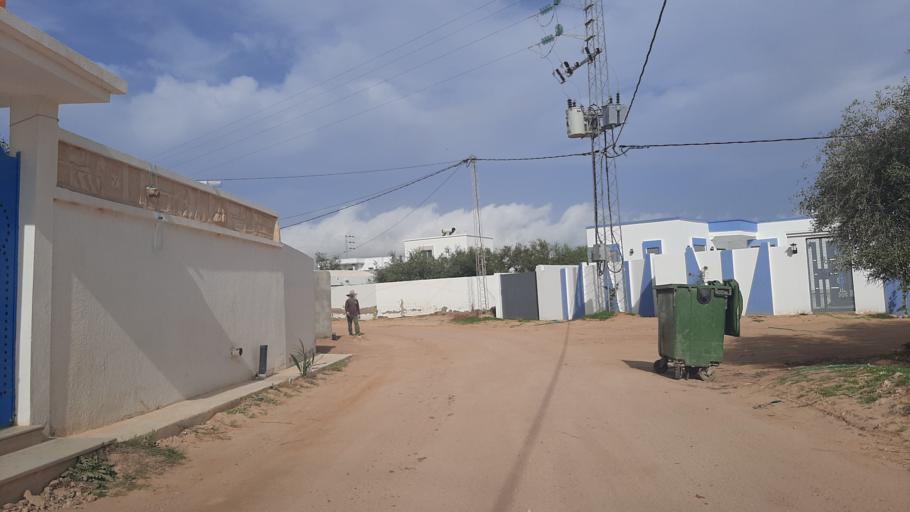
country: TN
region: Madanin
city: Midoun
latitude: 33.8007
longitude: 11.0274
